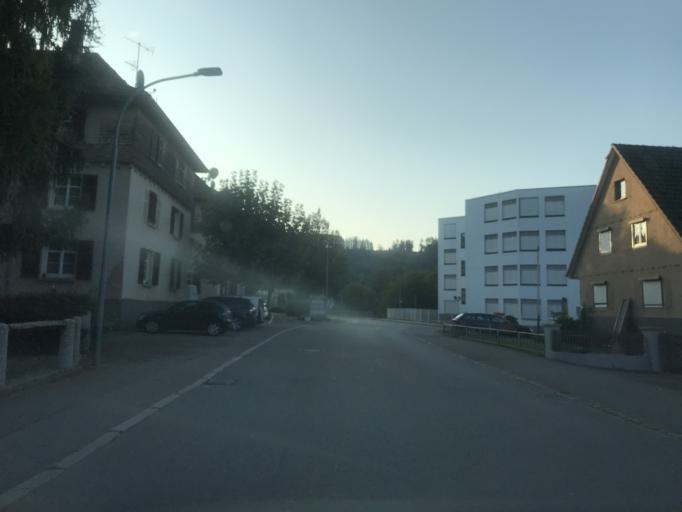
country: DE
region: Baden-Wuerttemberg
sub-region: Freiburg Region
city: Hausen
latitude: 47.6802
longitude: 7.8435
